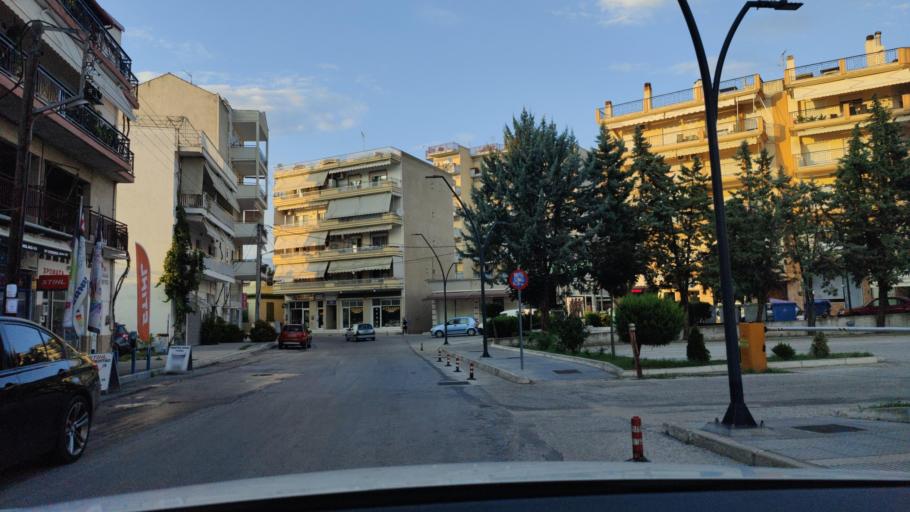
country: GR
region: Central Macedonia
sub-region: Nomos Serron
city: Sidirokastro
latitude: 41.2361
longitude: 23.3902
